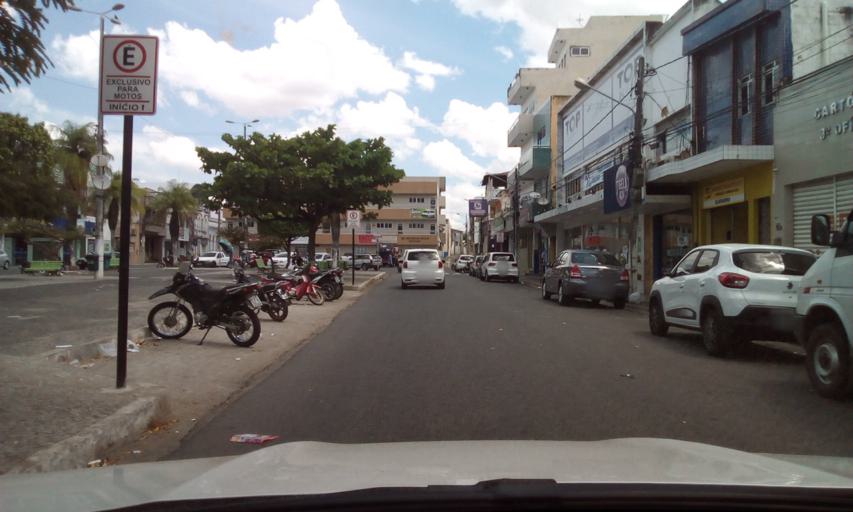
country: BR
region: Paraiba
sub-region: Guarabira
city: Guarabira
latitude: -6.8541
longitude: -35.4894
